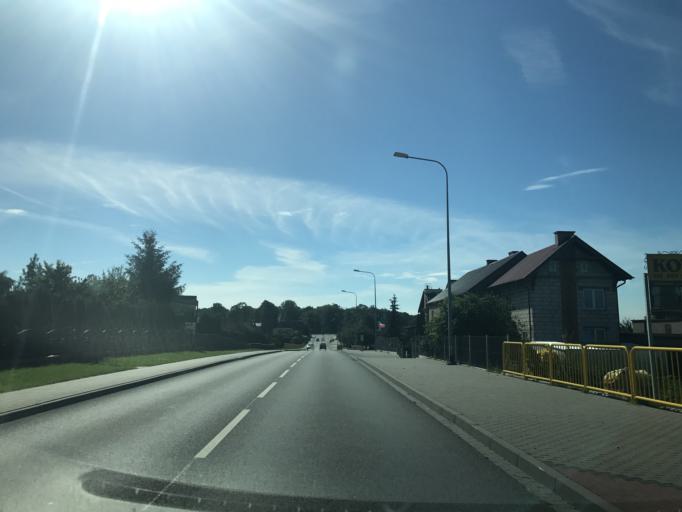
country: PL
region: Pomeranian Voivodeship
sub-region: Powiat chojnicki
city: Chojnice
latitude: 53.6834
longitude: 17.6356
